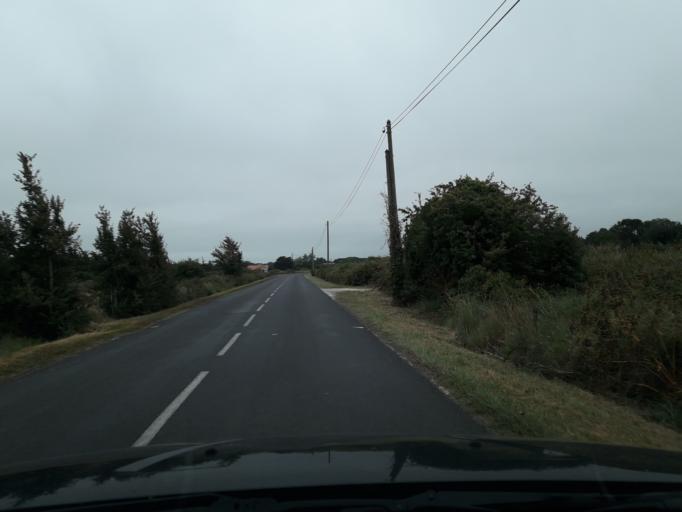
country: FR
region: Poitou-Charentes
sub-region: Departement de la Charente-Maritime
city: Boyard-Ville
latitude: 45.9566
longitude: -1.2488
